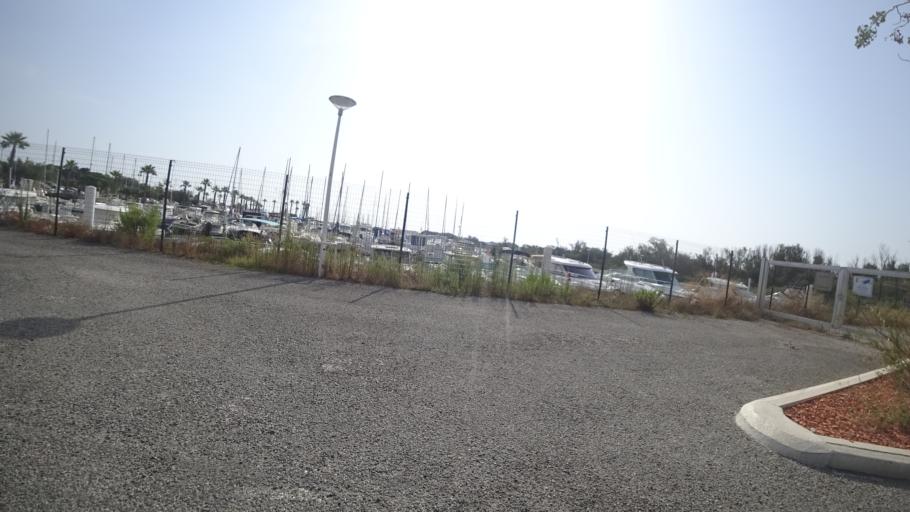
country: FR
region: Languedoc-Roussillon
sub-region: Departement des Pyrenees-Orientales
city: Sainte-Marie-Plage
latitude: 42.7220
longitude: 3.0347
